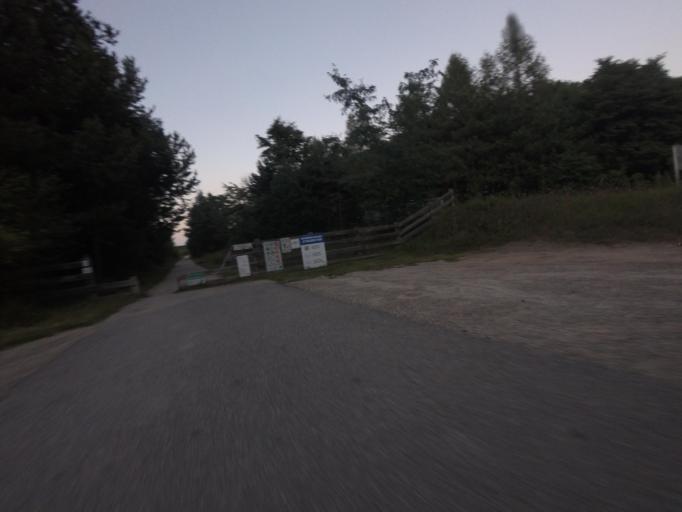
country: CA
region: Ontario
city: Bradford West Gwillimbury
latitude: 43.9613
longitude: -79.8271
